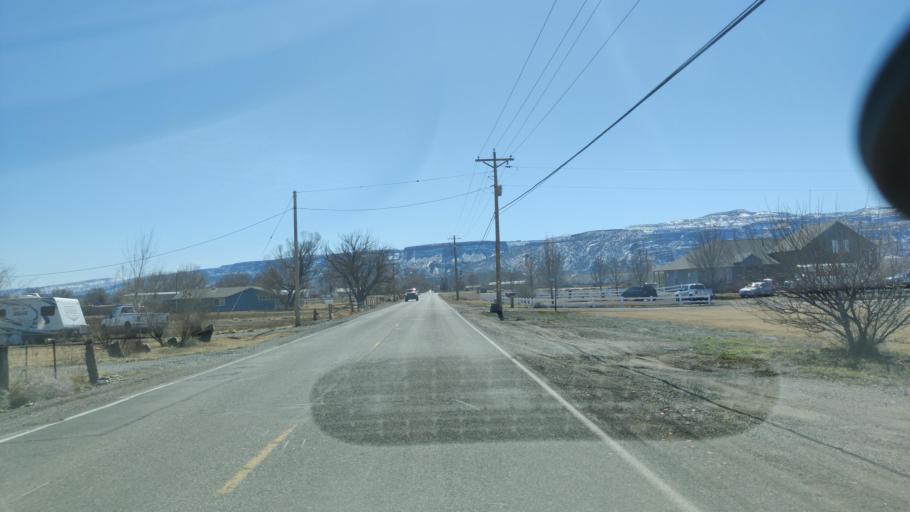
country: US
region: Colorado
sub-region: Mesa County
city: Fruita
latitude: 39.1459
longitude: -108.7011
